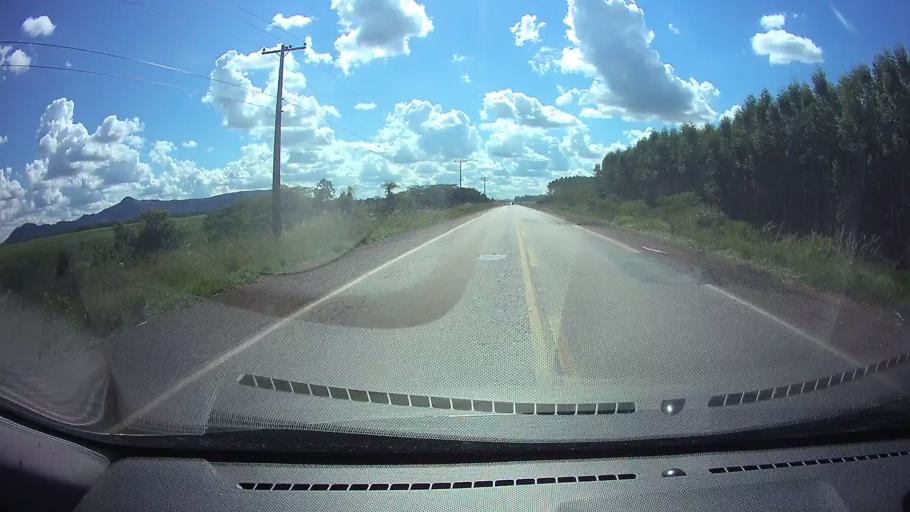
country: PY
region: Guaira
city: Coronel Martinez
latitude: -25.7603
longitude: -56.7480
